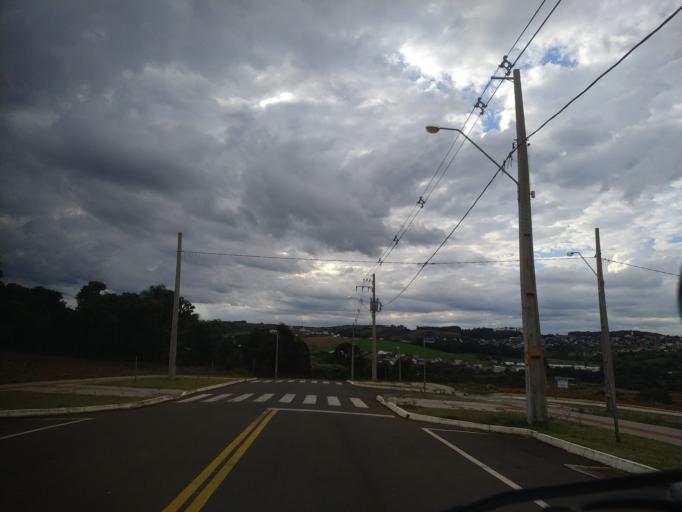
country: BR
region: Santa Catarina
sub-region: Chapeco
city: Chapeco
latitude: -27.0631
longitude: -52.6235
